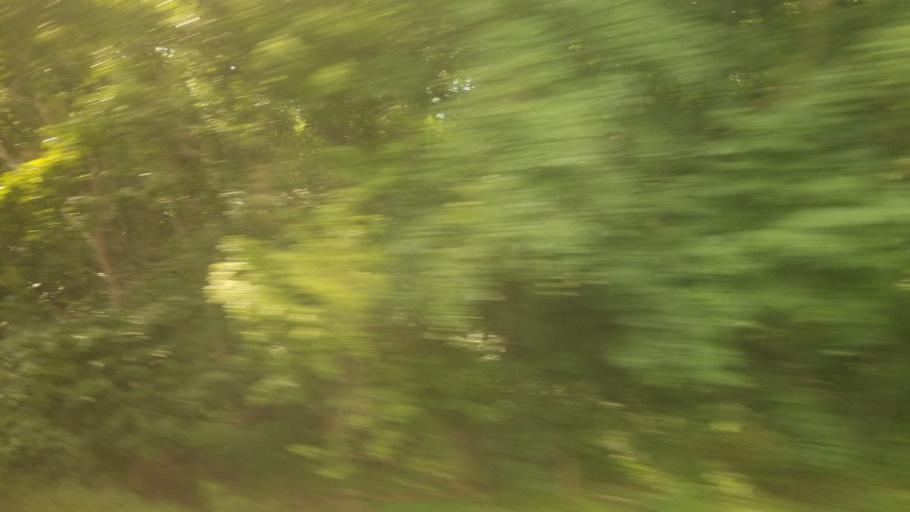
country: US
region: Kansas
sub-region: Johnson County
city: De Soto
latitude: 38.9788
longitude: -95.0108
